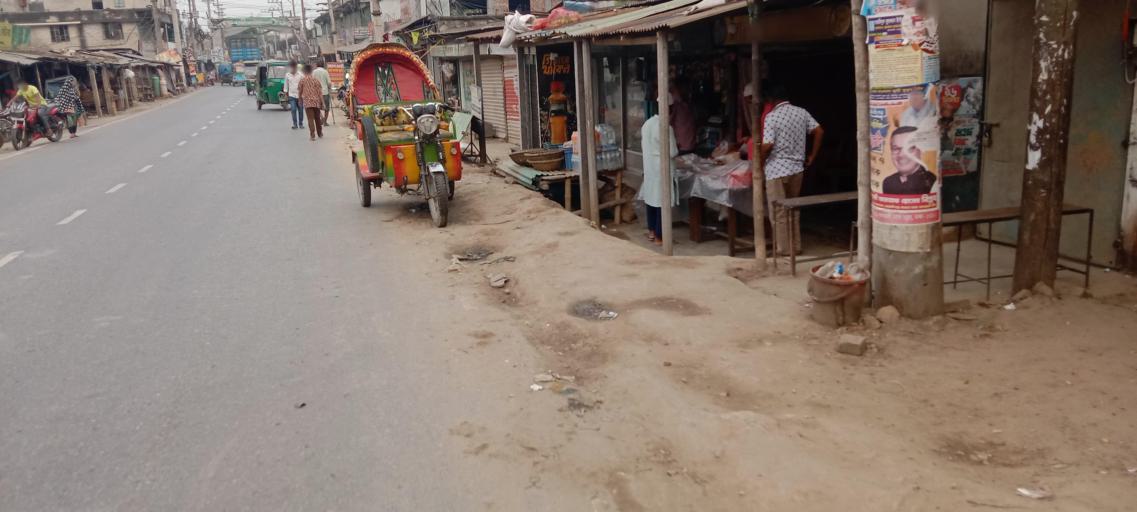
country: BD
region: Dhaka
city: Azimpur
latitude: 23.6979
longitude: 90.3424
